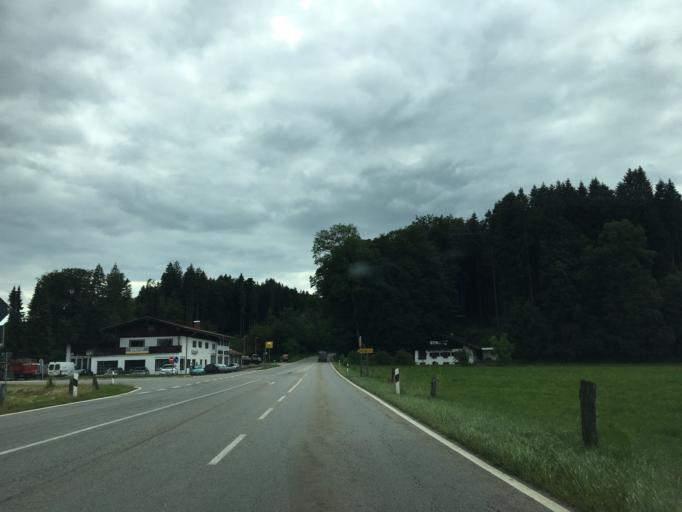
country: DE
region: Bavaria
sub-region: Upper Bavaria
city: Gmund am Tegernsee
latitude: 47.7772
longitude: 11.7582
